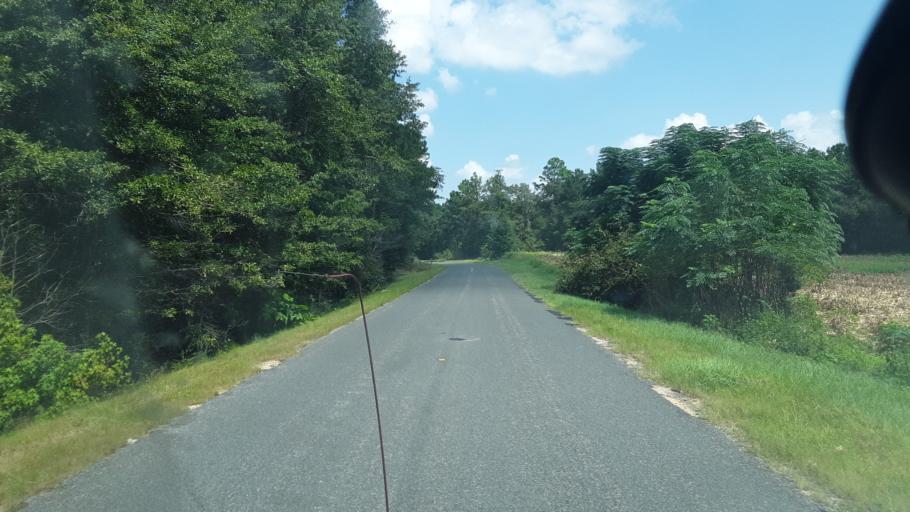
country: US
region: South Carolina
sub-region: Calhoun County
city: Oak Grove
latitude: 33.6827
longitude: -80.9693
